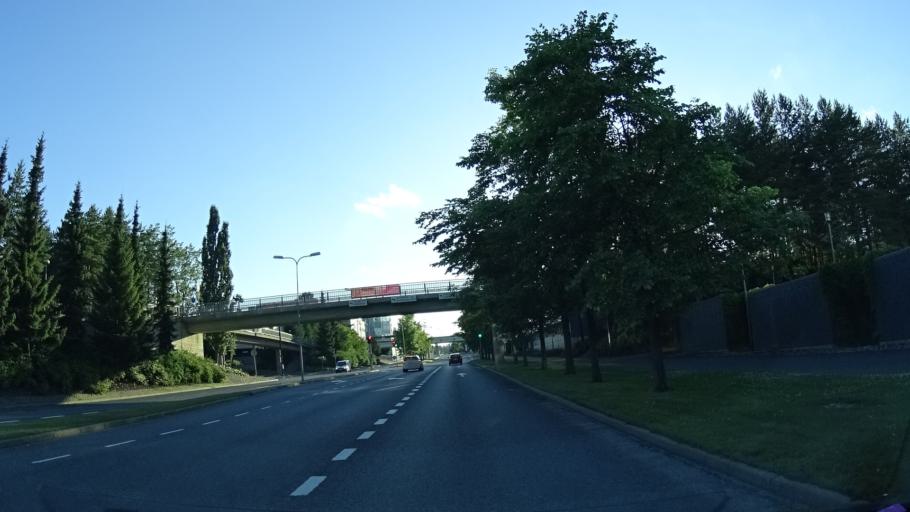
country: FI
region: Uusimaa
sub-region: Helsinki
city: Teekkarikylae
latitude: 60.2639
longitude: 24.8579
